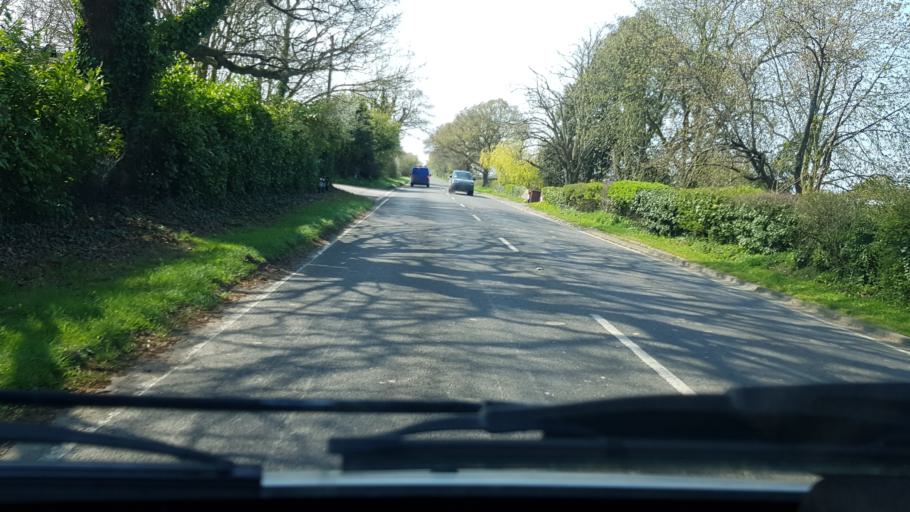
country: GB
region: England
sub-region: West Sussex
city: Birdham
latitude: 50.7986
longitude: -0.8170
